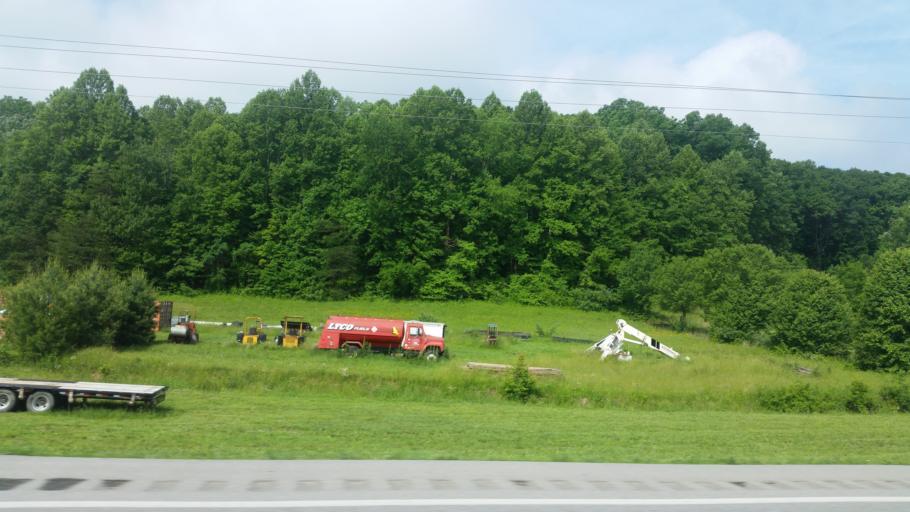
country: US
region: Kentucky
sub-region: Rowan County
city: Morehead
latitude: 38.2484
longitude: -83.5197
